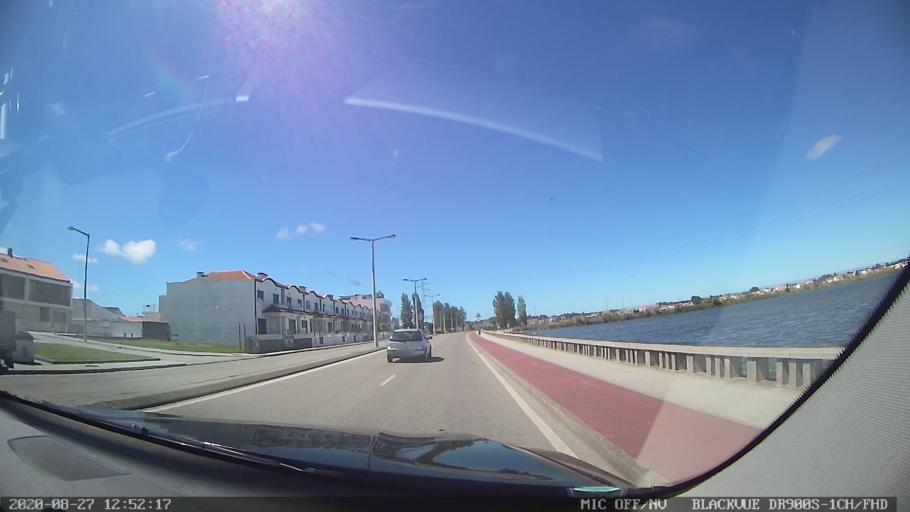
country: PT
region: Aveiro
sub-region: Ilhavo
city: Ilhavo
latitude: 40.6072
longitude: -8.6764
